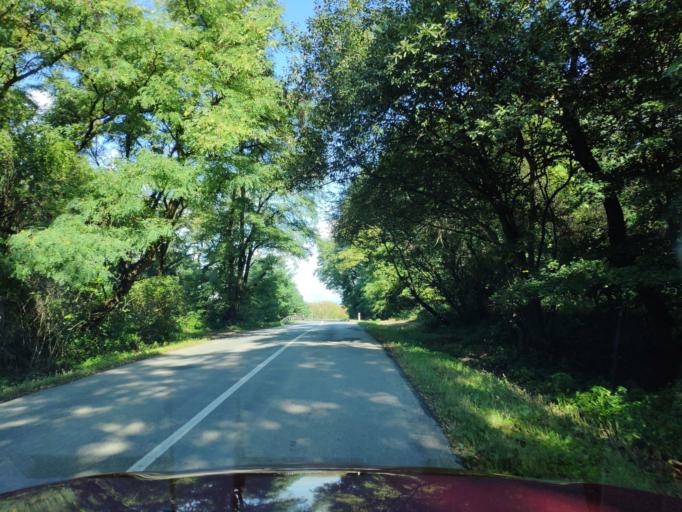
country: SK
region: Presovsky
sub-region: Okres Presov
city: Presov
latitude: 48.8849
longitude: 21.2648
